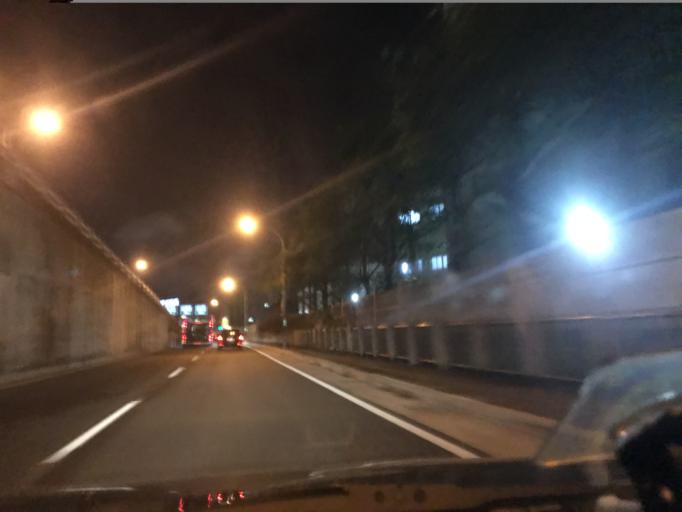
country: TW
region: Taiwan
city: Taoyuan City
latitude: 24.9852
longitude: 121.2378
